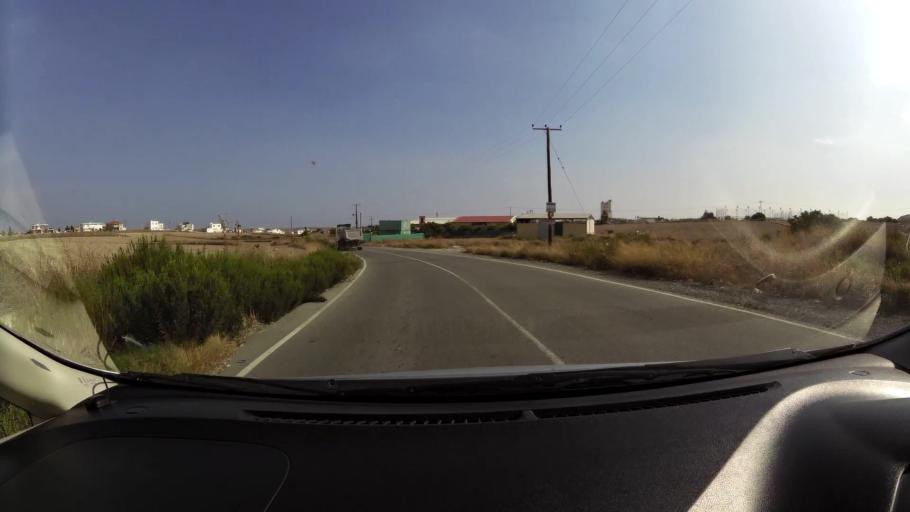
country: CY
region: Larnaka
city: Dhromolaxia
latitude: 34.9065
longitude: 33.5752
